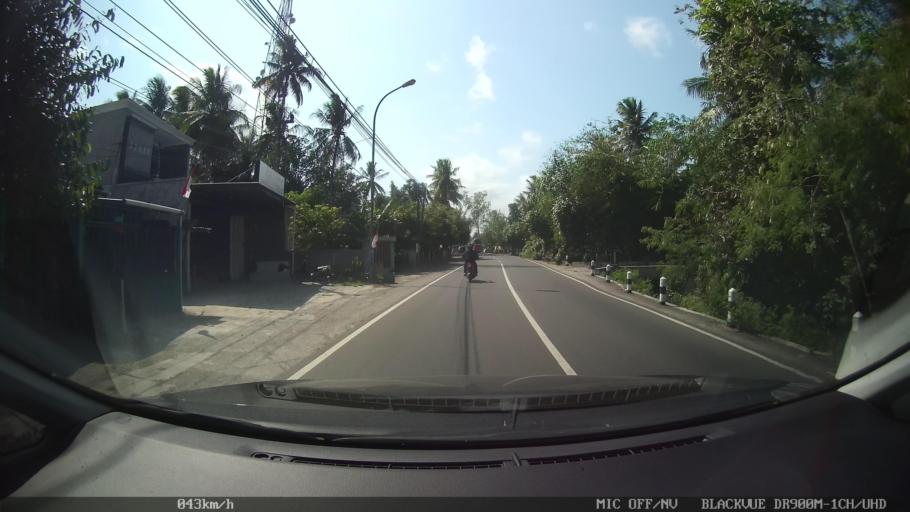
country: ID
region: Daerah Istimewa Yogyakarta
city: Srandakan
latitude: -7.9398
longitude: 110.2318
